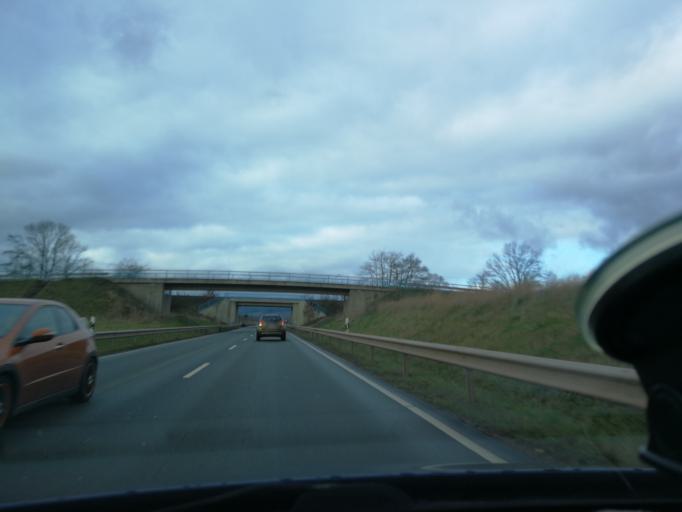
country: DE
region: Rheinland-Pfalz
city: Altrich
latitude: 49.9648
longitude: 6.9298
